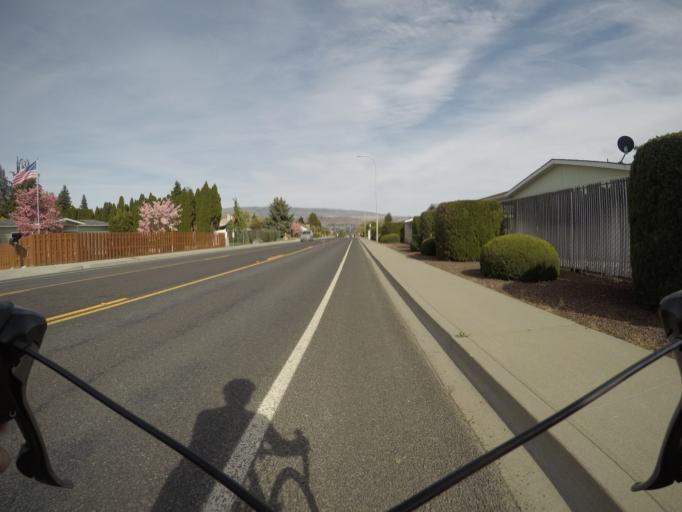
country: US
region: Washington
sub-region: Chelan County
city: West Wenatchee
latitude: 47.4424
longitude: -120.3439
